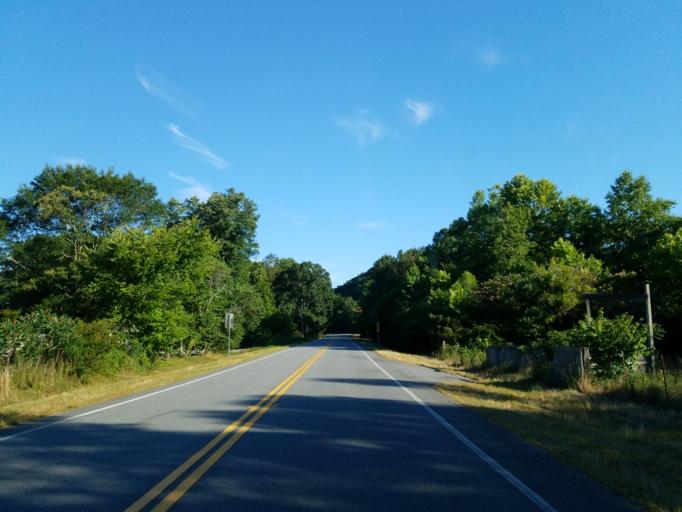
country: US
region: Georgia
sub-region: Gordon County
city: Calhoun
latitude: 34.6067
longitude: -85.0447
